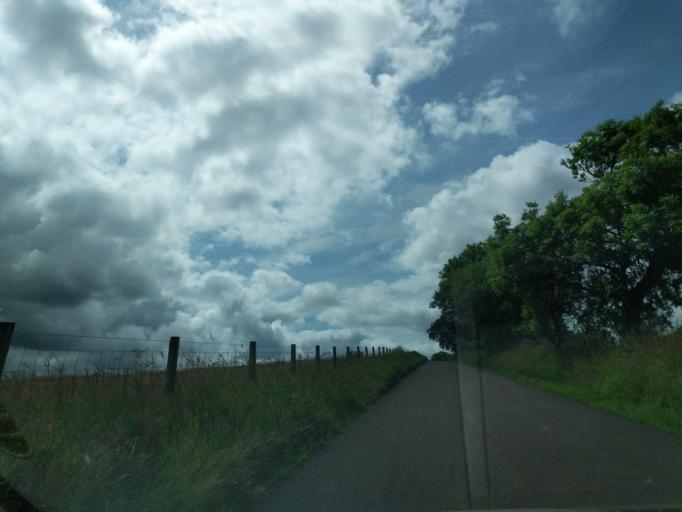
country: GB
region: Scotland
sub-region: South Lanarkshire
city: Carnwath
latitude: 55.6270
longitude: -3.6804
